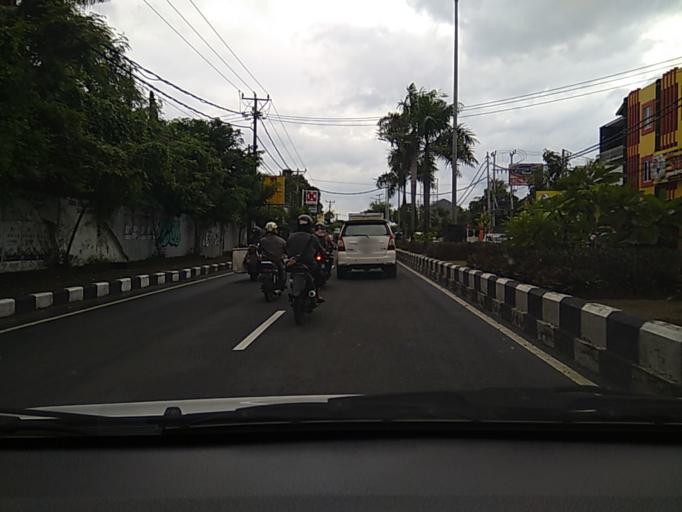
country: ID
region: Bali
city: Bualu
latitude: -8.7844
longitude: 115.1910
